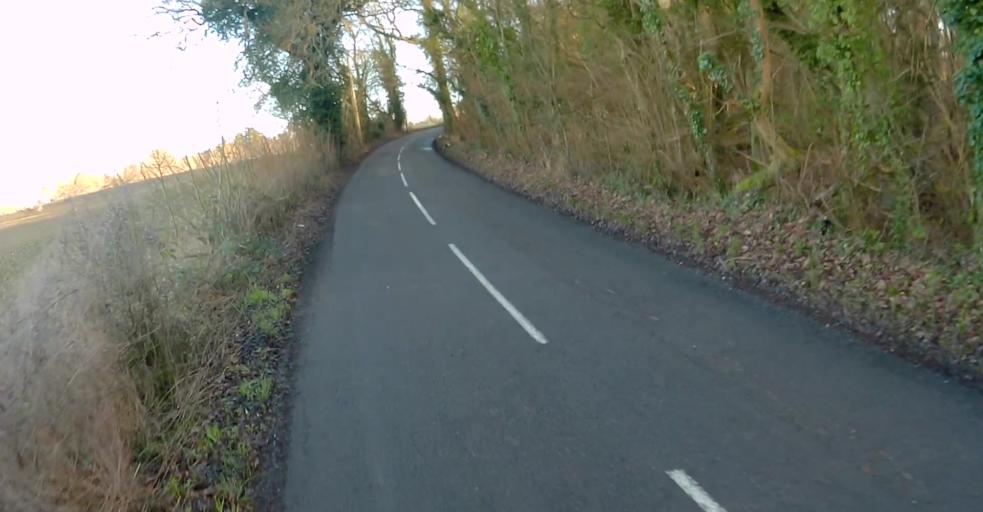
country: GB
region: England
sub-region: Hampshire
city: Hook
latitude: 51.2841
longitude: -0.9964
